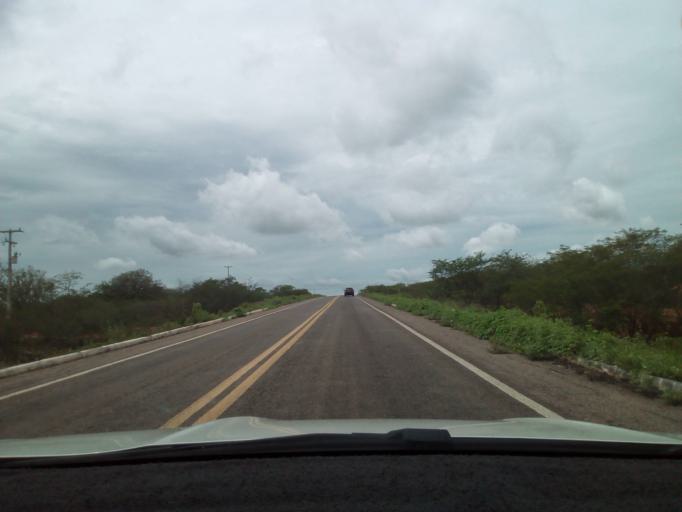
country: BR
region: Rio Grande do Norte
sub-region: Patu
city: Patu
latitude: -6.1483
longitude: -37.7520
